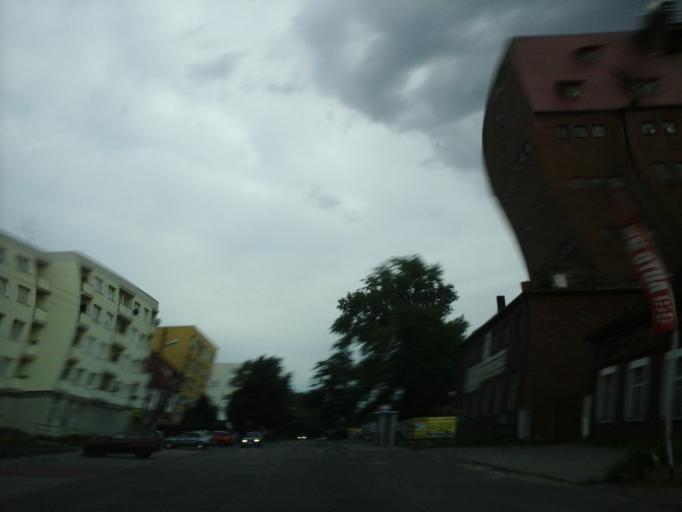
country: PL
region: West Pomeranian Voivodeship
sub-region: Powiat goleniowski
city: Nowogard
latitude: 53.6659
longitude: 15.1254
